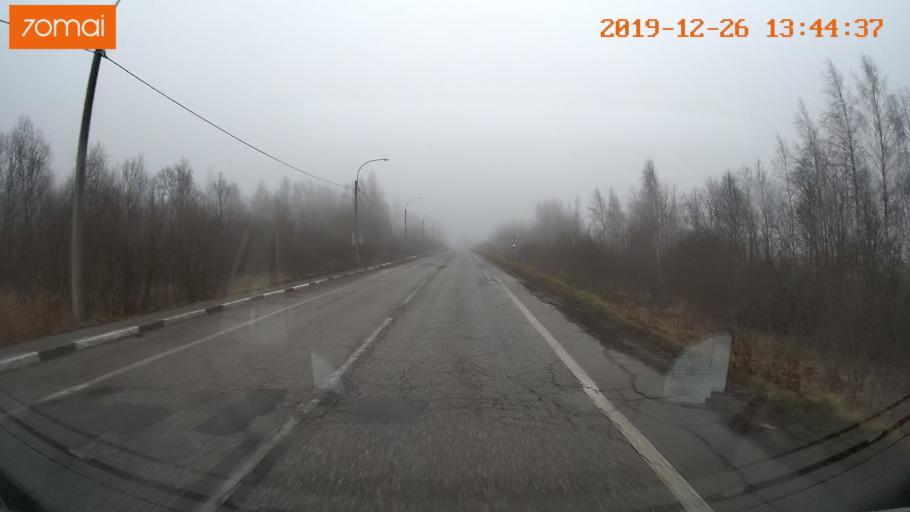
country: RU
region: Vologda
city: Sheksna
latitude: 58.7005
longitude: 38.5089
